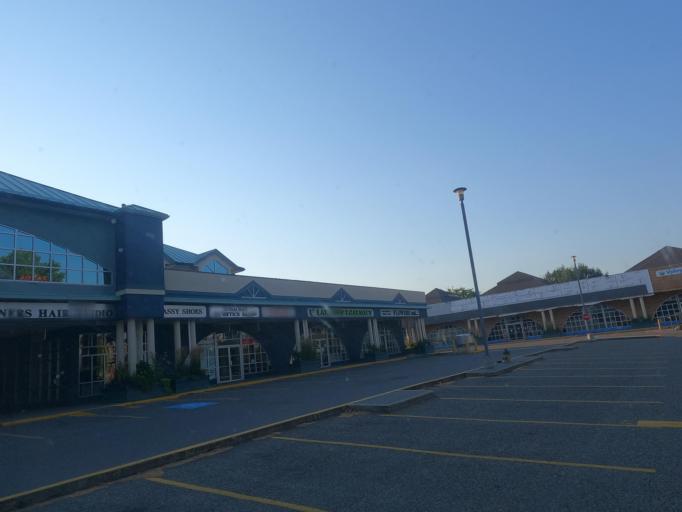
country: CA
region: British Columbia
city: Kelowna
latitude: 49.8717
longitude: -119.4752
